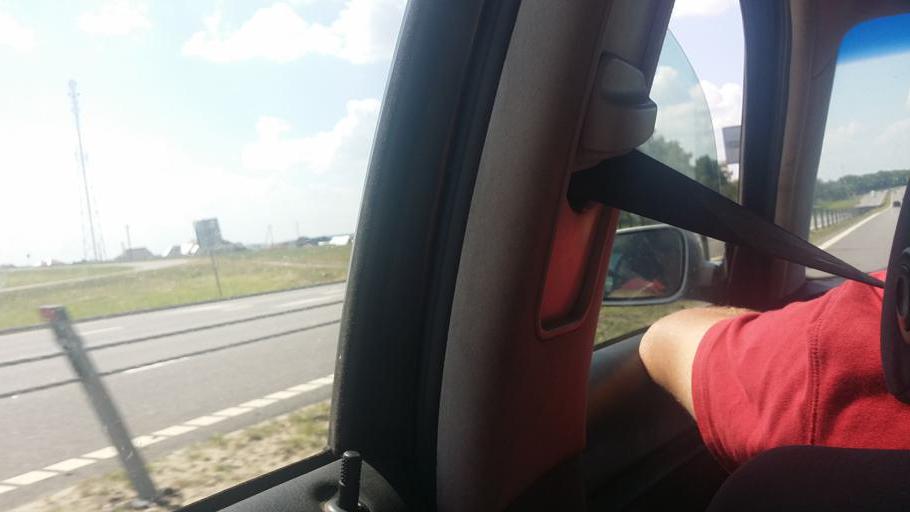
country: BY
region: Minsk
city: Smilavichy
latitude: 53.7614
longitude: 28.0539
